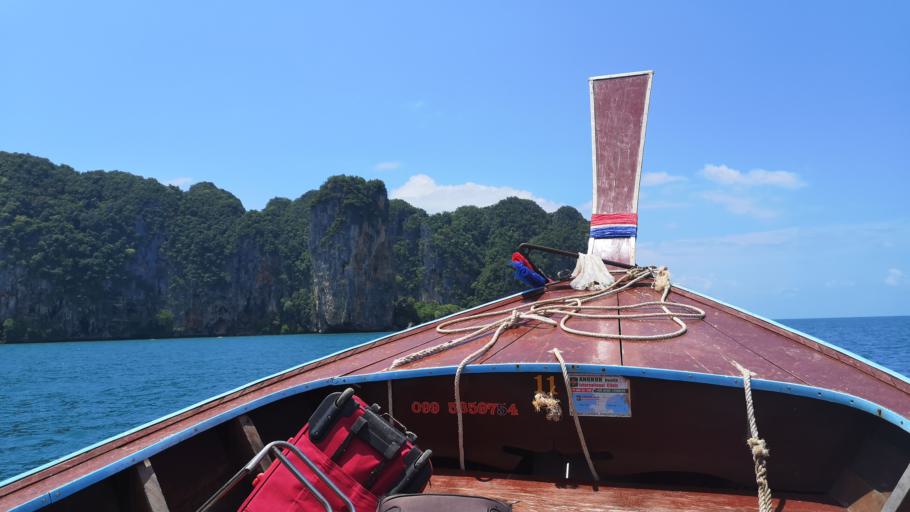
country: TH
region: Phangnga
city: Ban Ao Nang
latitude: 8.0214
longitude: 98.8224
